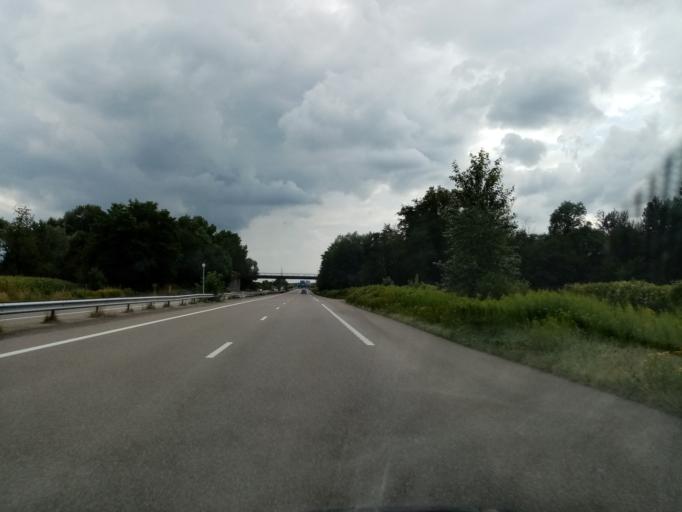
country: FR
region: Alsace
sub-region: Departement du Bas-Rhin
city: Soufflenheim
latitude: 48.8296
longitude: 8.0062
